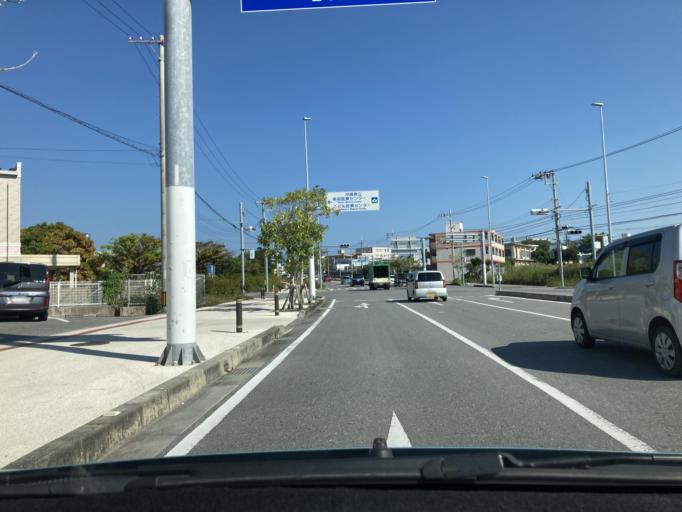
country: JP
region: Okinawa
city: Naha-shi
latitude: 26.2048
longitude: 127.7234
